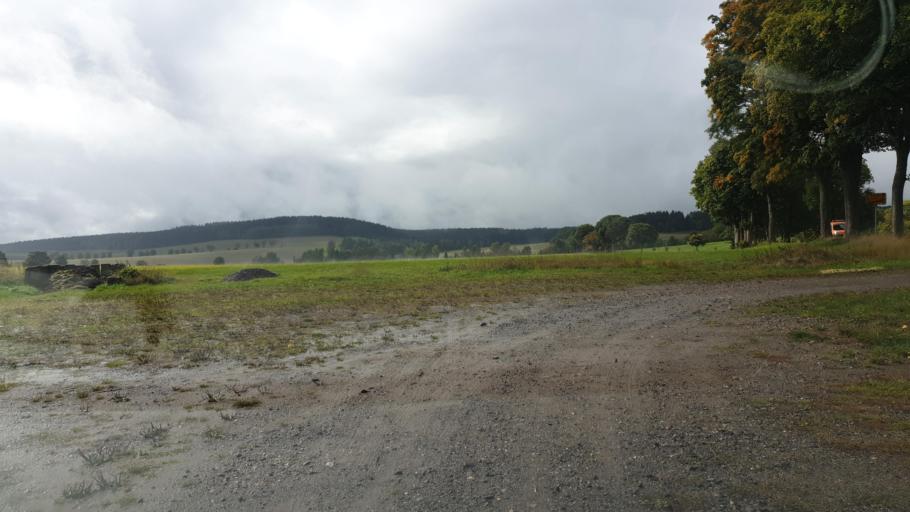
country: DE
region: Saxony
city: Rechenberg-Bienenmuhle
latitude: 50.7104
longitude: 13.4973
